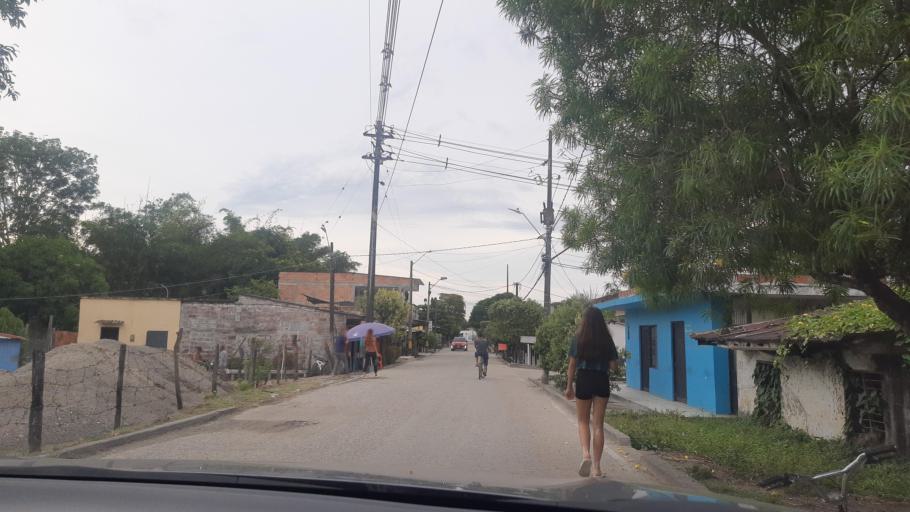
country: CO
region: Antioquia
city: Puerto Triunfo
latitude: 5.8744
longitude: -74.6389
